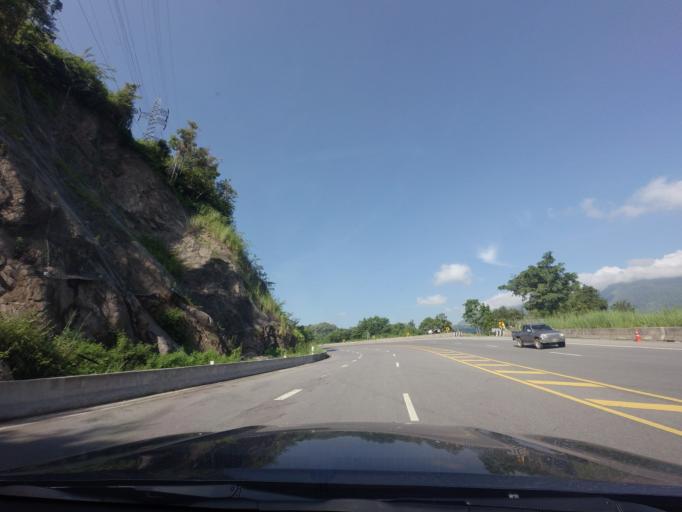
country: TH
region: Phetchabun
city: Khao Kho
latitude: 16.7776
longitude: 101.0819
